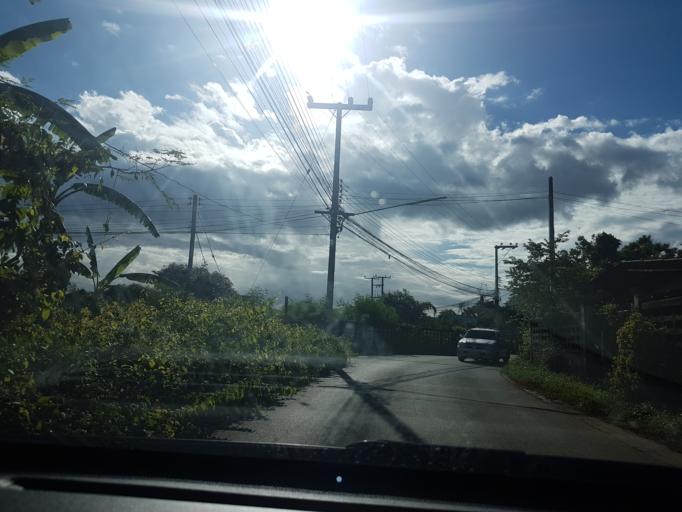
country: TH
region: Lampang
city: Ko Kha
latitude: 18.2331
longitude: 99.4265
